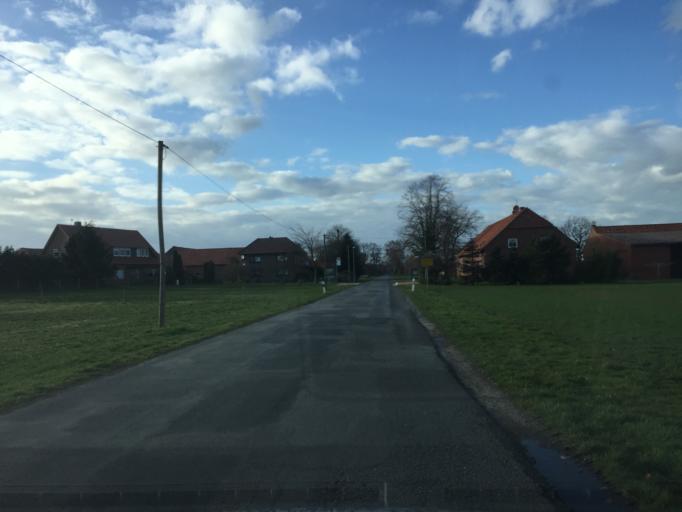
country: DE
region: Lower Saxony
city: Uchte
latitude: 52.5485
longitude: 8.9390
